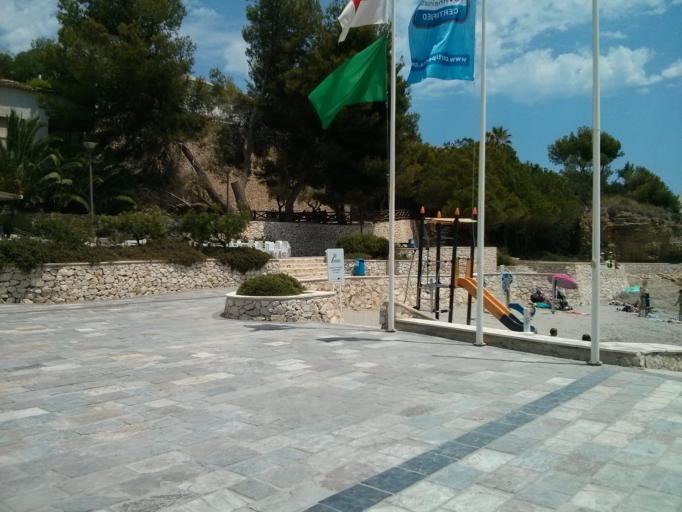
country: ES
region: Valencia
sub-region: Provincia de Alicante
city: Calp
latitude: 38.6649
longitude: 0.0878
